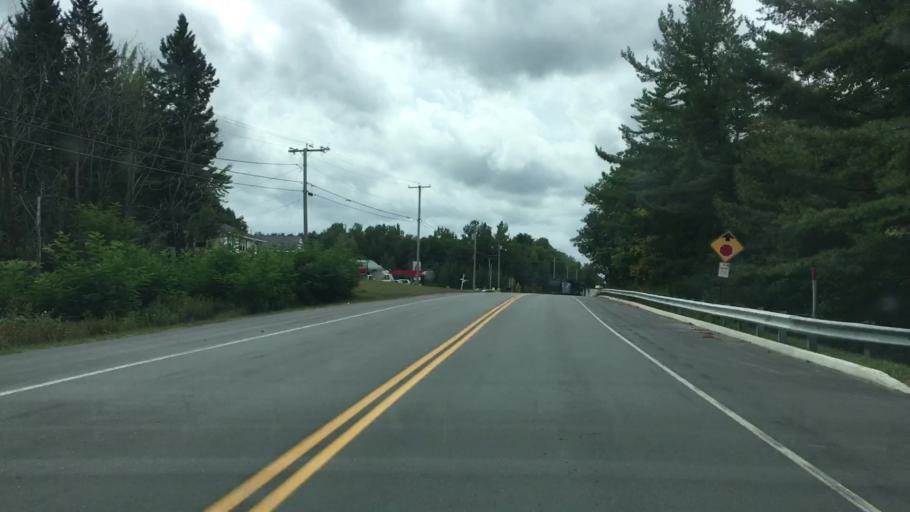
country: US
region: Maine
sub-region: Penobscot County
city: Milford
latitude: 44.9544
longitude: -68.6982
